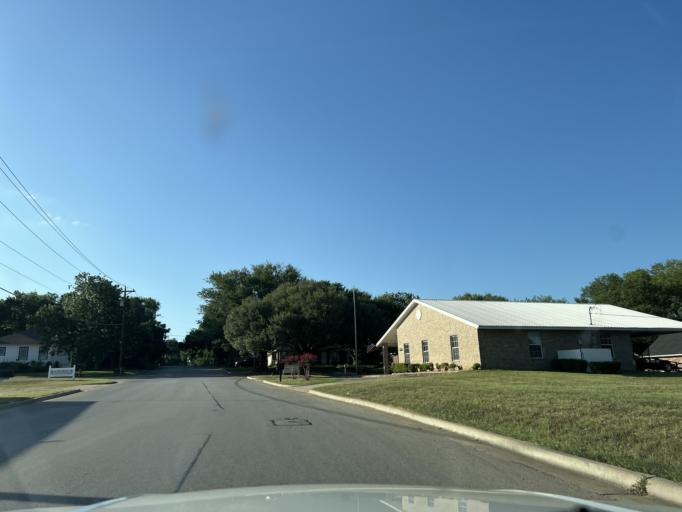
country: US
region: Texas
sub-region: Washington County
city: Brenham
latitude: 30.1508
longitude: -96.3848
